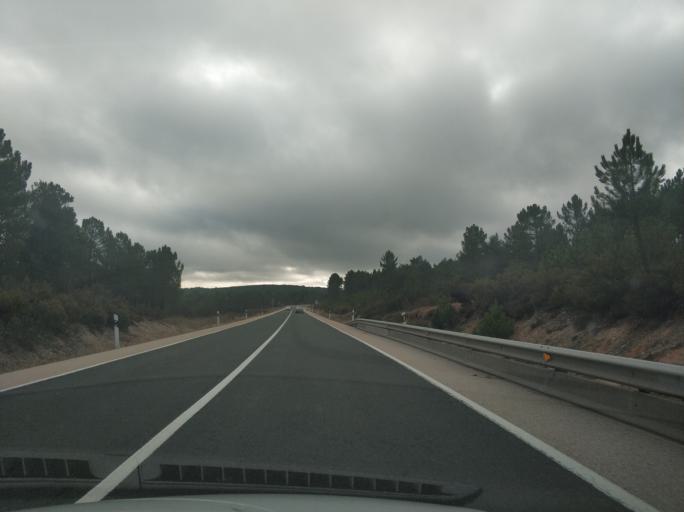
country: ES
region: Castille and Leon
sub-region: Provincia de Soria
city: Muriel Viejo
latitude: 41.8240
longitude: -2.9436
